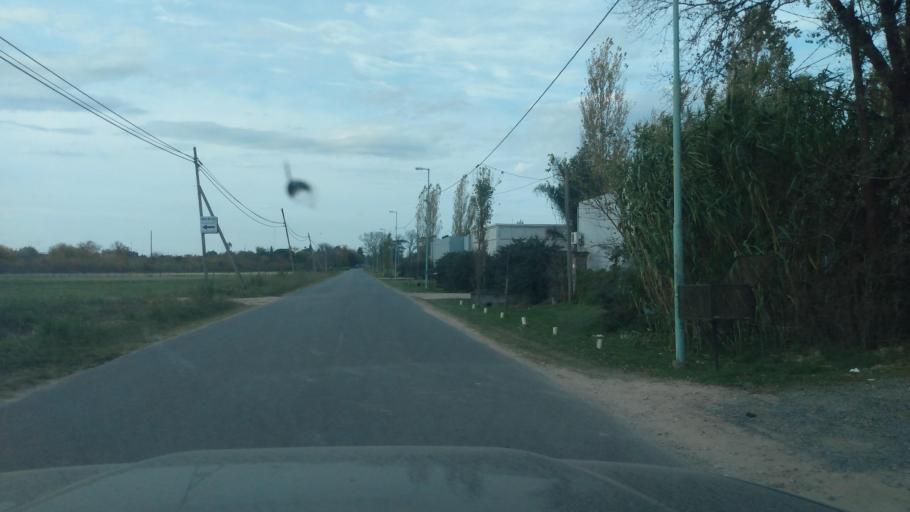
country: AR
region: Buenos Aires
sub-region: Partido de Lujan
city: Lujan
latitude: -34.5840
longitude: -59.1272
